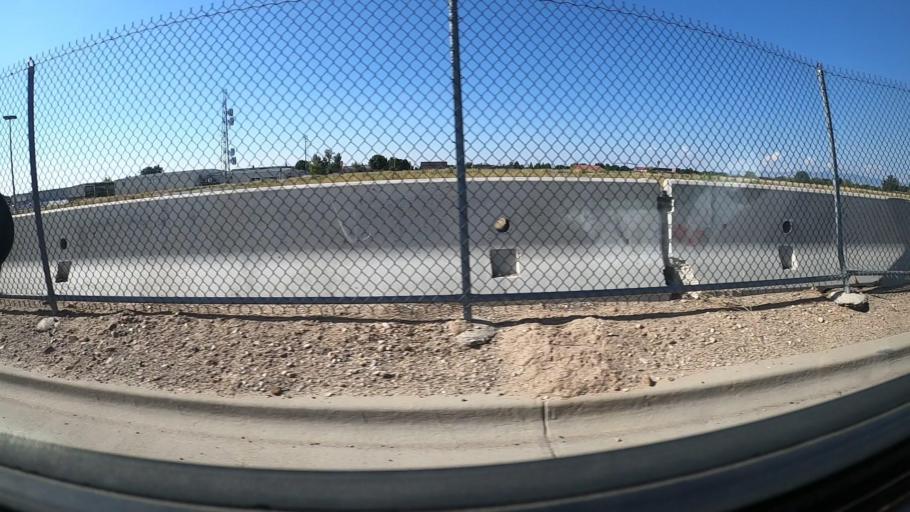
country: US
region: Idaho
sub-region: Ada County
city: Meridian
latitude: 43.5962
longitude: -116.3787
